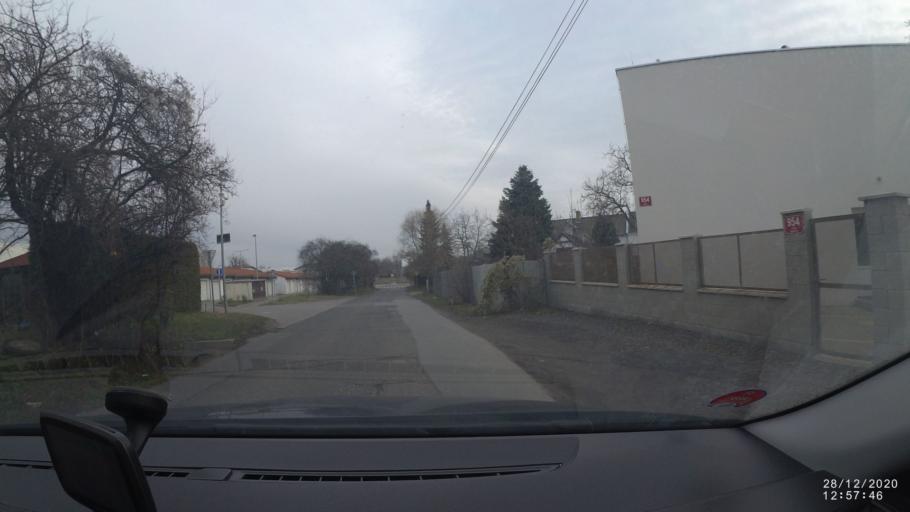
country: CZ
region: Praha
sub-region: Praha 19
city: Satalice
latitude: 50.1520
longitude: 14.5892
